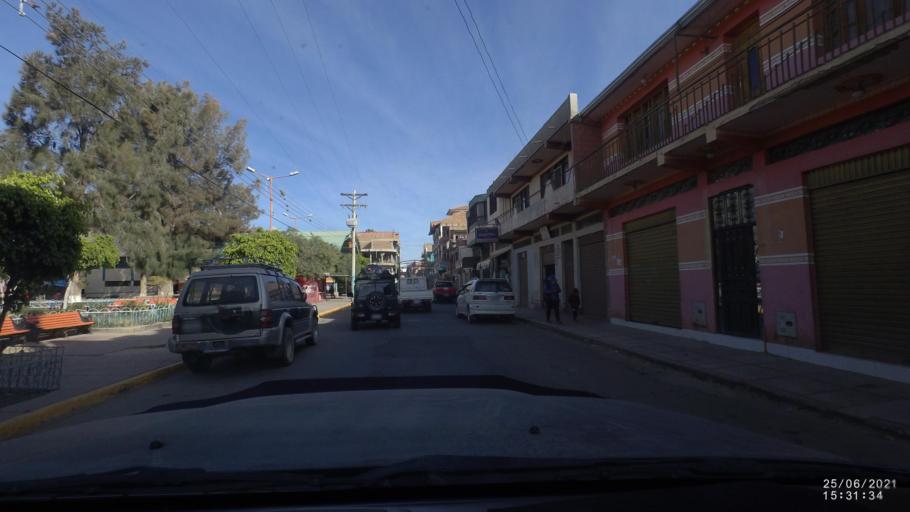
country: BO
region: Cochabamba
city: Cliza
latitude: -17.5903
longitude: -65.9344
